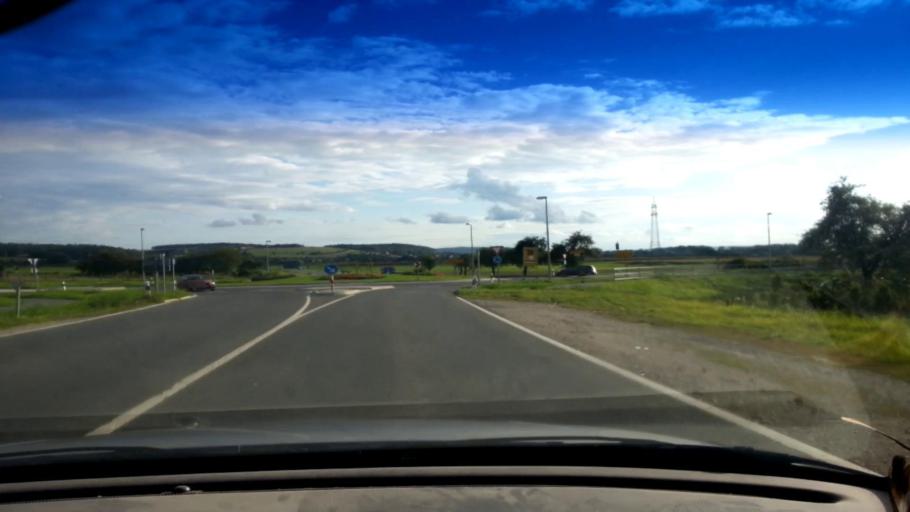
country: DE
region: Bavaria
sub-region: Upper Franconia
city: Ebensfeld
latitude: 50.0600
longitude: 10.9561
